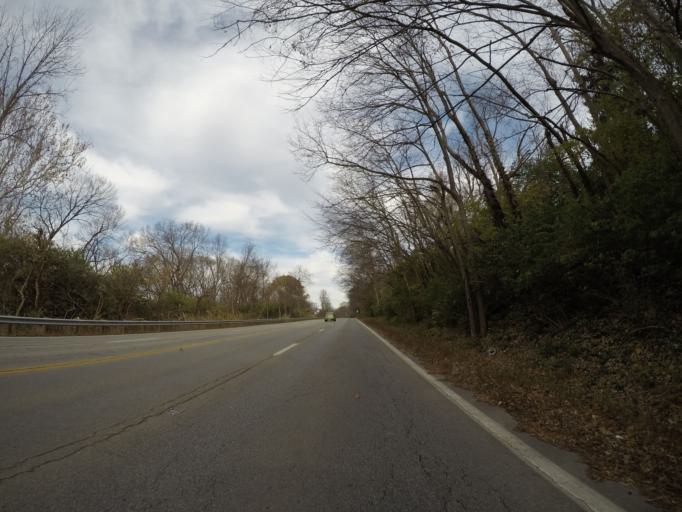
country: US
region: Ohio
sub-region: Franklin County
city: Upper Arlington
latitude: 40.0095
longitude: -83.0869
